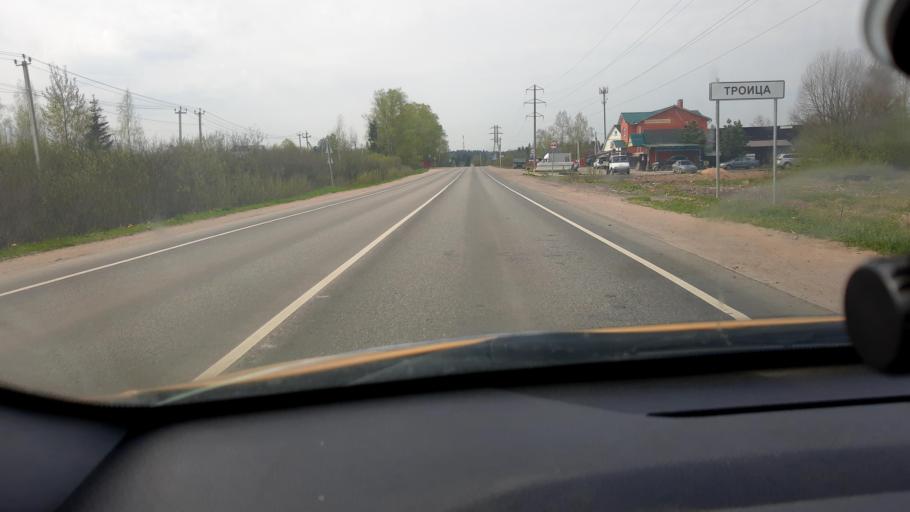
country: RU
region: Moskovskaya
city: Rumyantsevo
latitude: 55.9091
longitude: 36.5878
